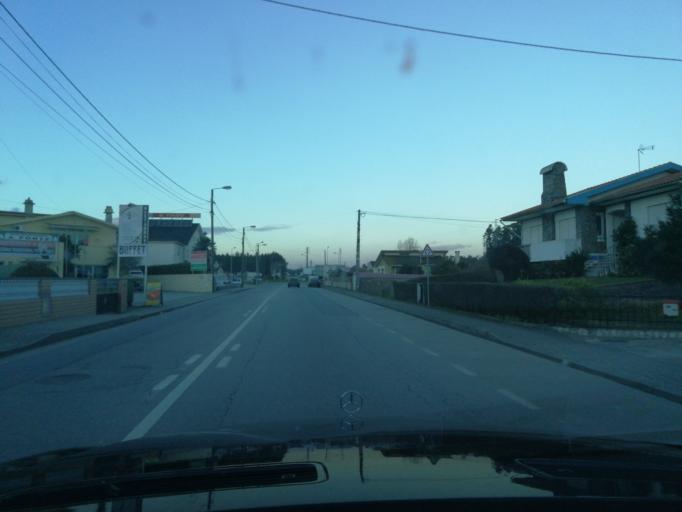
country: PT
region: Aveiro
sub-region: Estarreja
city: Beduido
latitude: 40.7681
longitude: -8.5709
